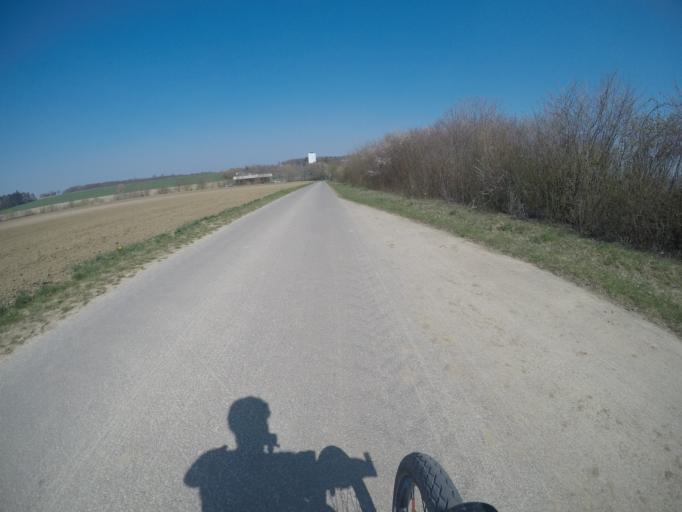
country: DE
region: Baden-Wuerttemberg
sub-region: Regierungsbezirk Stuttgart
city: Renningen
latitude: 48.7405
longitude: 8.9230
